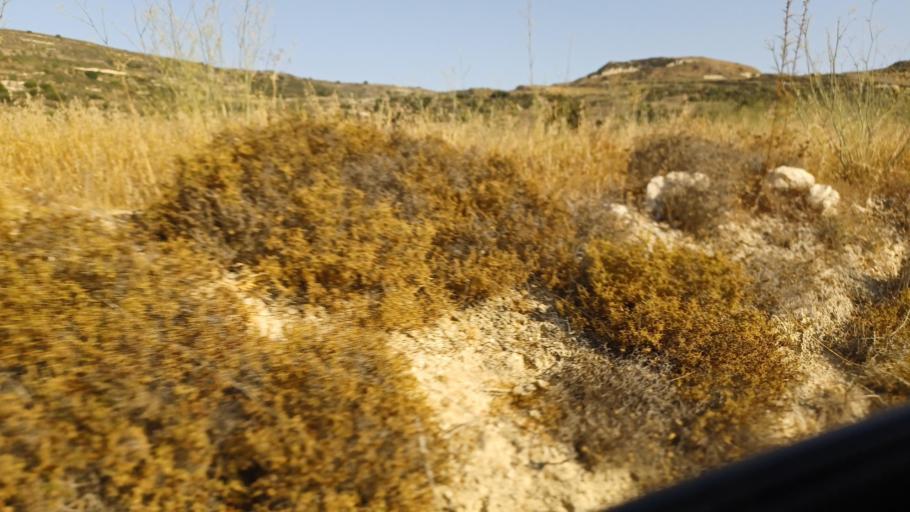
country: CY
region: Pafos
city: Tala
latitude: 34.8910
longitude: 32.4511
